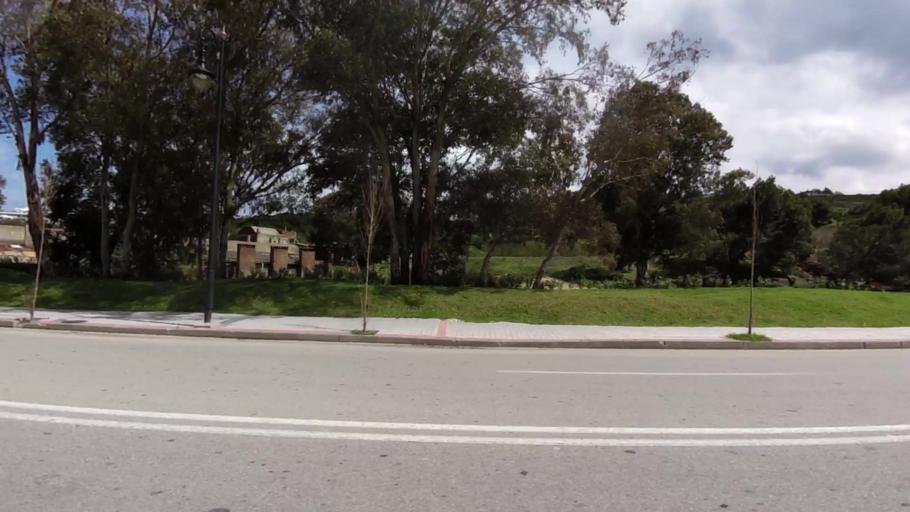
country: MA
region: Tanger-Tetouan
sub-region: Tanger-Assilah
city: Tangier
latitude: 35.7748
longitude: -5.7623
